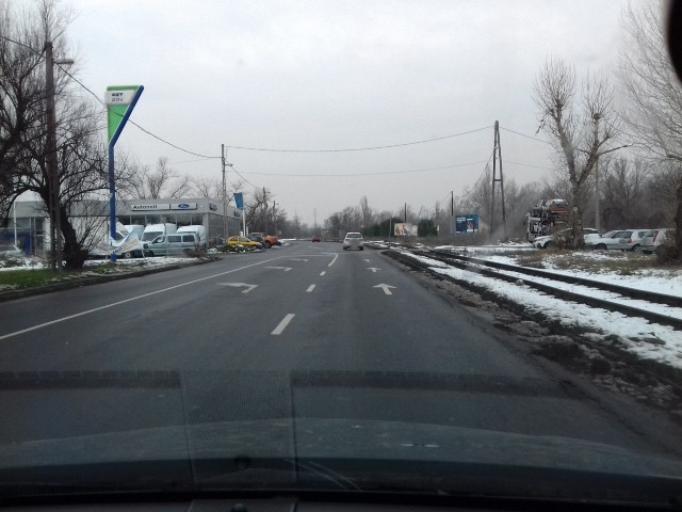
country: HU
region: Budapest
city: Budapest XXI. keruelet
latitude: 47.4363
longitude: 19.0846
